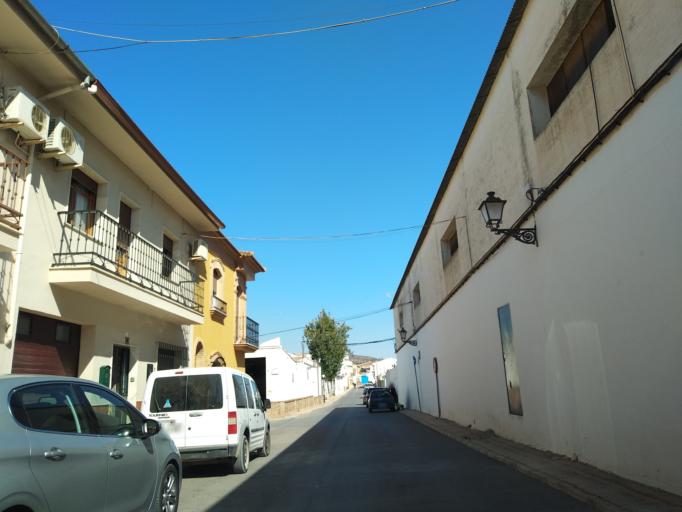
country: ES
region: Andalusia
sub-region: Provincia de Malaga
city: Mollina
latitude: 37.1273
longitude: -4.6565
